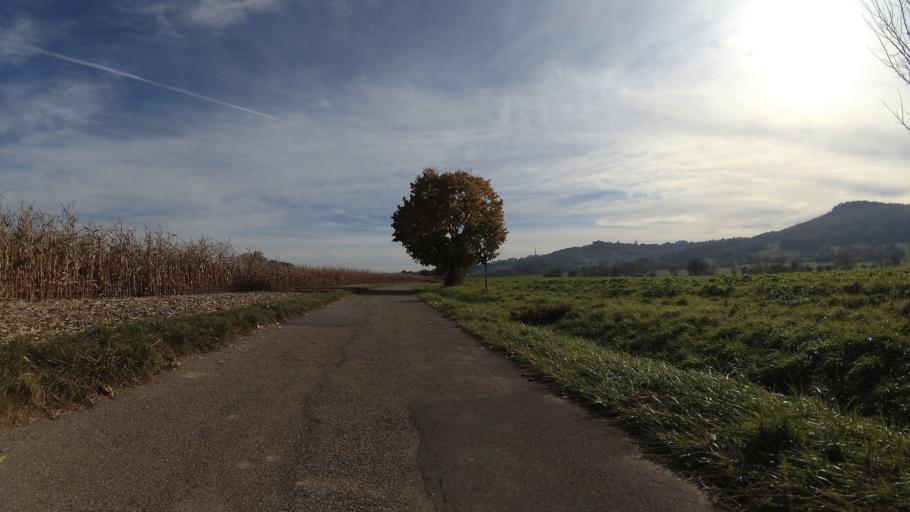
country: DE
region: Baden-Wuerttemberg
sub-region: Regierungsbezirk Stuttgart
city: Waldenburg
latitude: 49.2045
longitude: 9.6197
